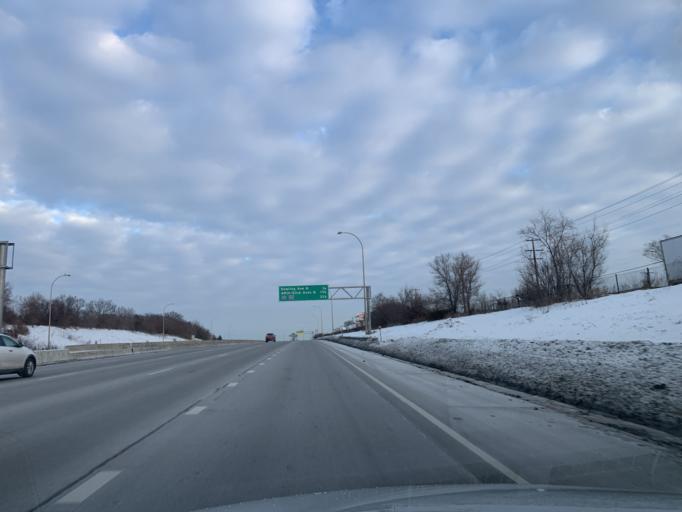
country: US
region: Minnesota
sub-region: Anoka County
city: Columbia Heights
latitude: 45.0152
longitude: -93.2823
